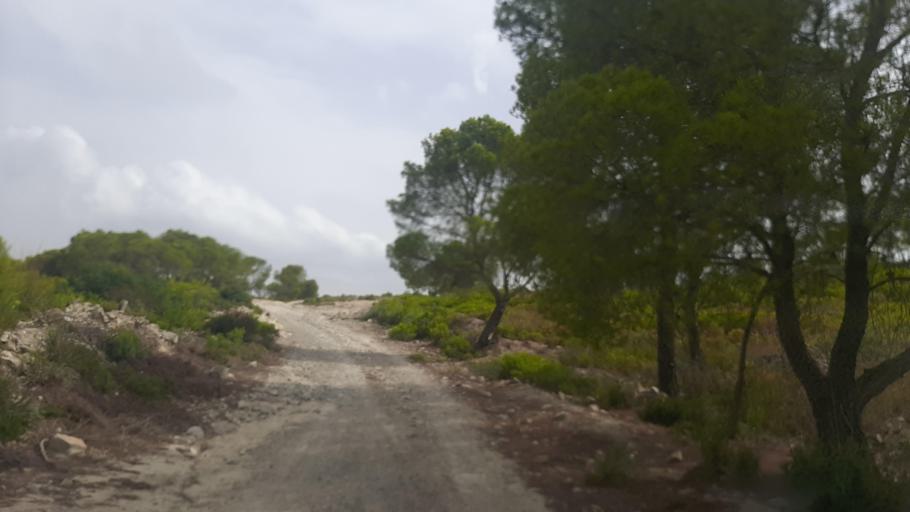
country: TN
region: Zaghwan
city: El Fahs
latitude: 36.1958
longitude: 9.8524
